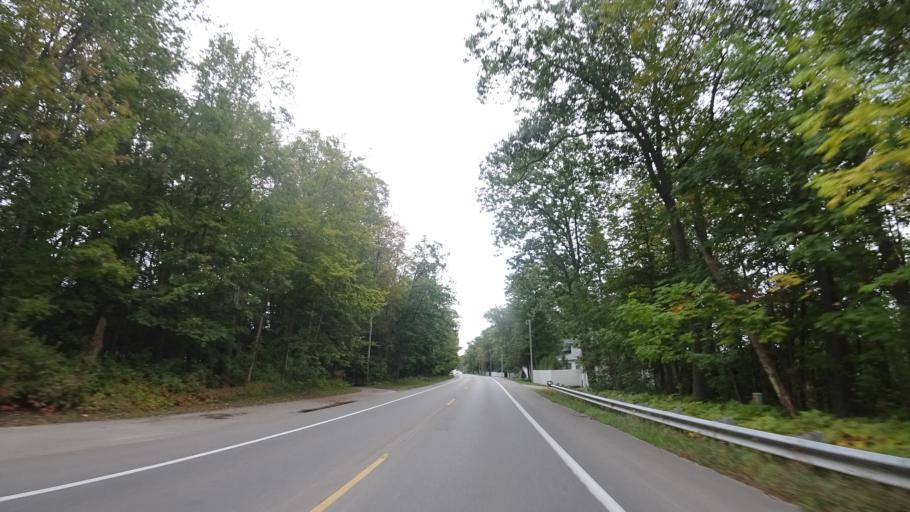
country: US
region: Michigan
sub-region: Emmet County
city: Harbor Springs
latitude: 45.4317
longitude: -84.9659
